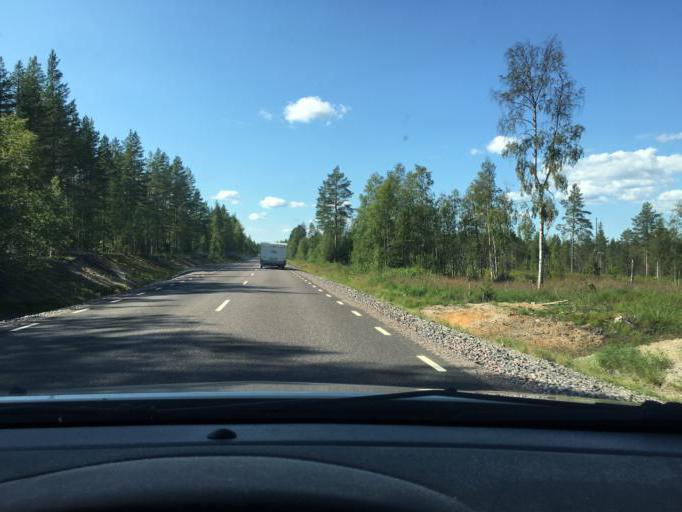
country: SE
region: Norrbotten
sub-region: Lulea Kommun
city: Ranea
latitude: 66.0494
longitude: 22.2317
